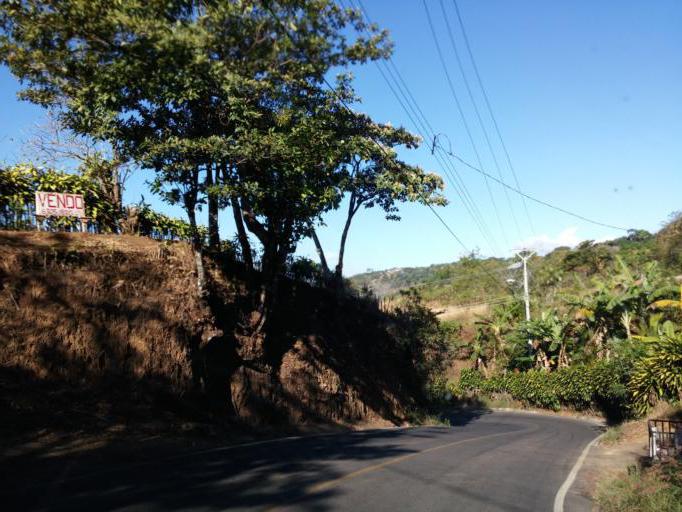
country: CR
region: Alajuela
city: Sabanilla
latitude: 10.0593
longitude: -84.2101
